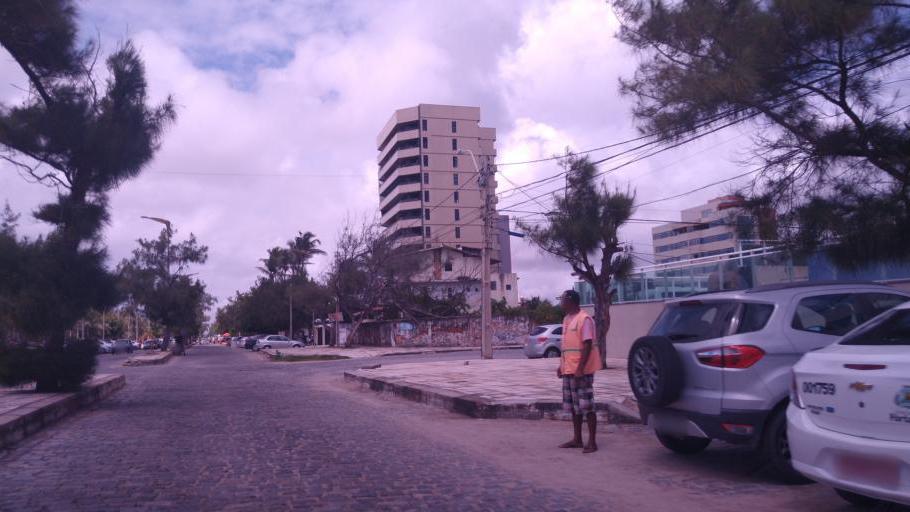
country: BR
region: Ceara
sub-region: Fortaleza
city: Fortaleza
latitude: -3.7317
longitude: -38.4575
